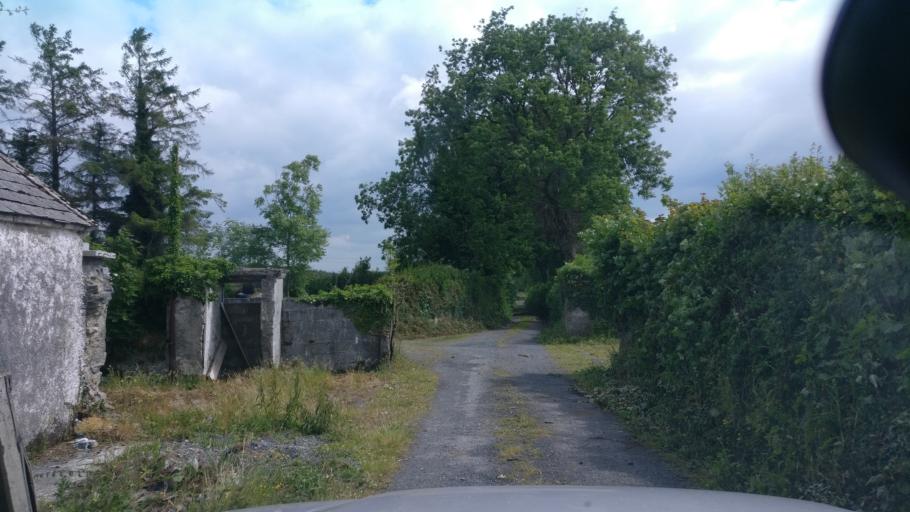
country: IE
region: Connaught
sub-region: County Galway
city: Ballinasloe
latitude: 53.2703
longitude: -8.3326
